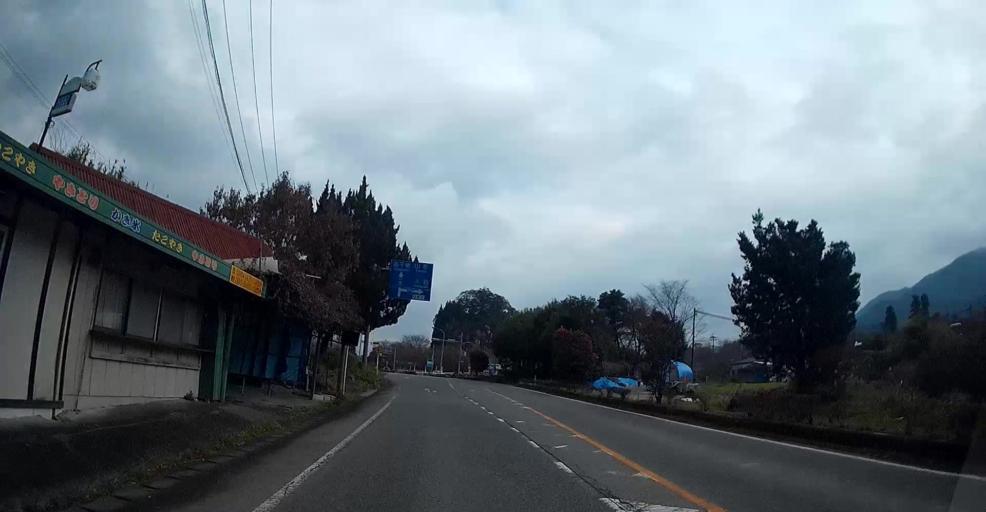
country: JP
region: Kumamoto
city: Matsubase
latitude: 32.6220
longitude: 130.8727
